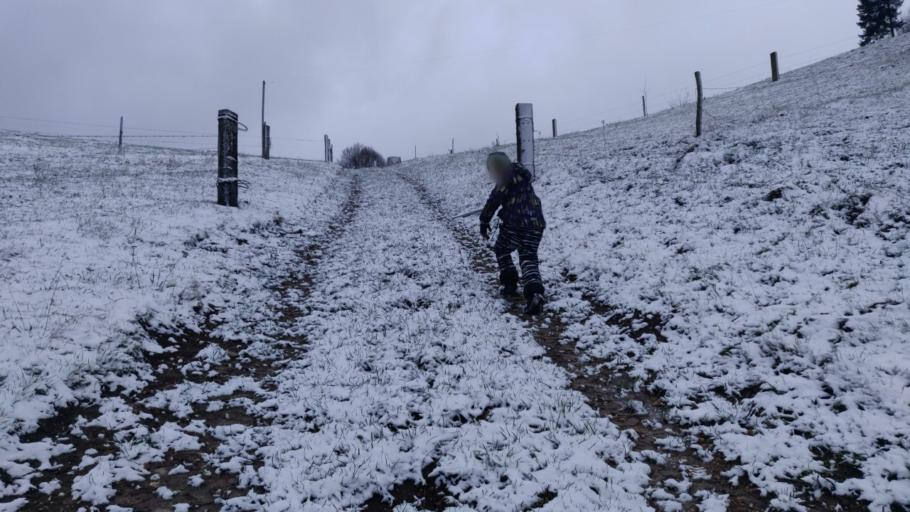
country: CH
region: Basel-Landschaft
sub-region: Bezirk Waldenburg
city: Langenbruck
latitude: 47.3588
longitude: 7.7665
